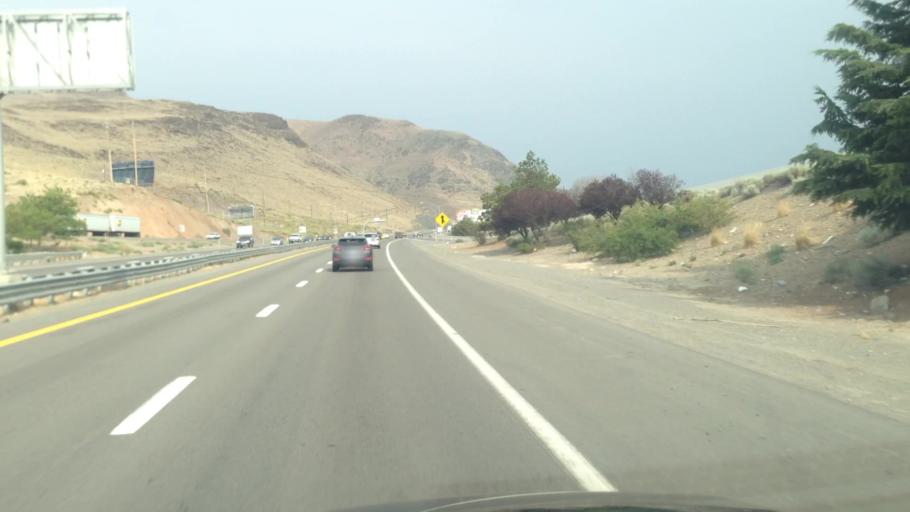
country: US
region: Nevada
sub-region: Washoe County
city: Sparks
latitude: 39.5262
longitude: -119.7005
